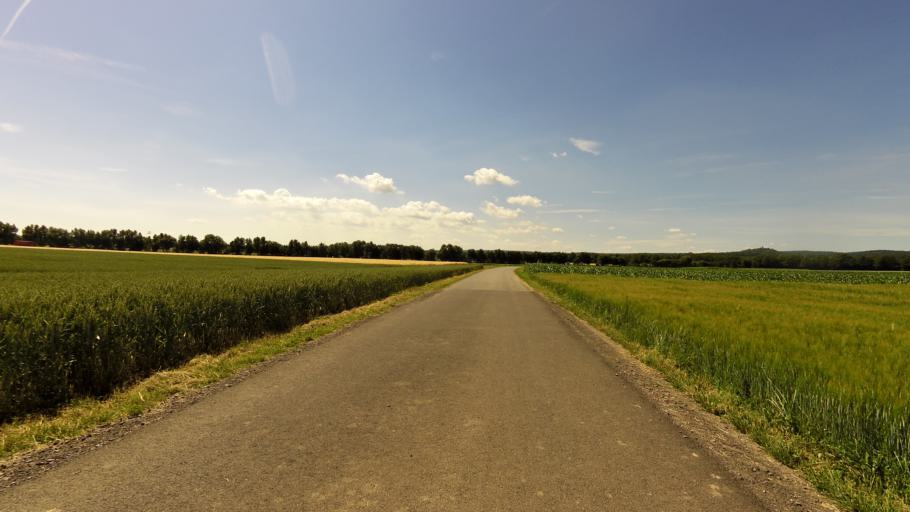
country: DE
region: North Rhine-Westphalia
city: Meckenheim
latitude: 50.6201
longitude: 6.9893
